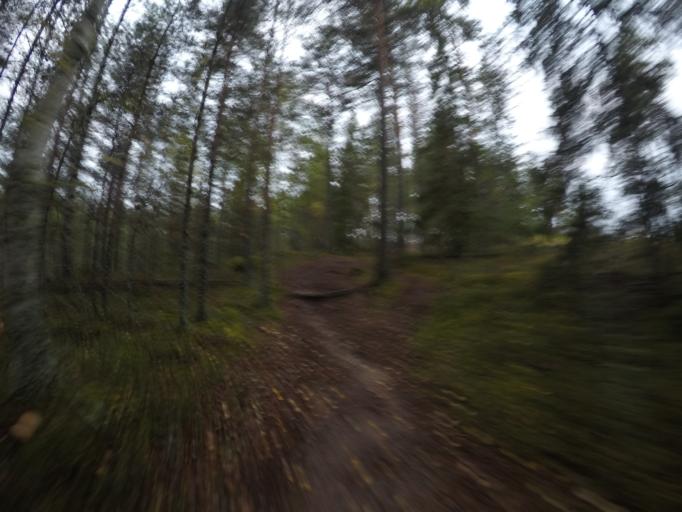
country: SE
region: Vaestmanland
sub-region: Kungsors Kommun
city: Kungsoer
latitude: 59.3818
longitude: 16.1130
